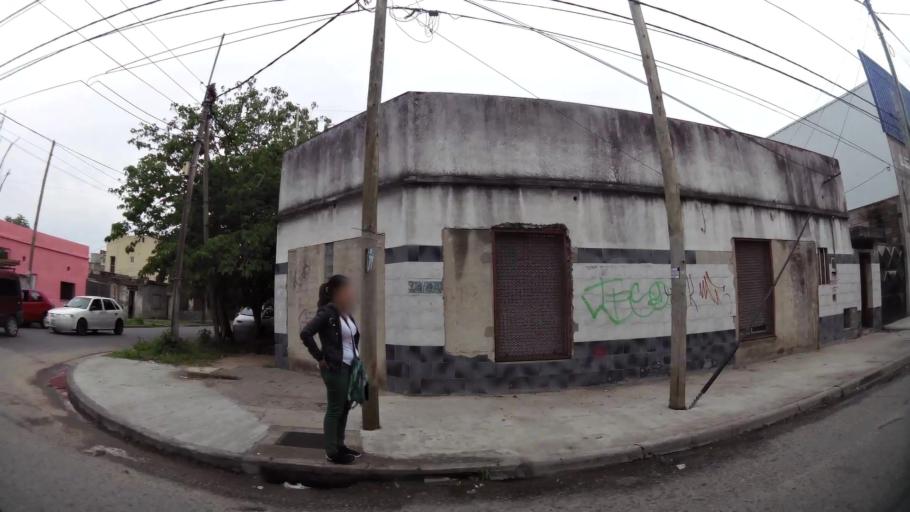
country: AR
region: Buenos Aires
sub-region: Partido de Lanus
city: Lanus
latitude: -34.7151
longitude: -58.3543
